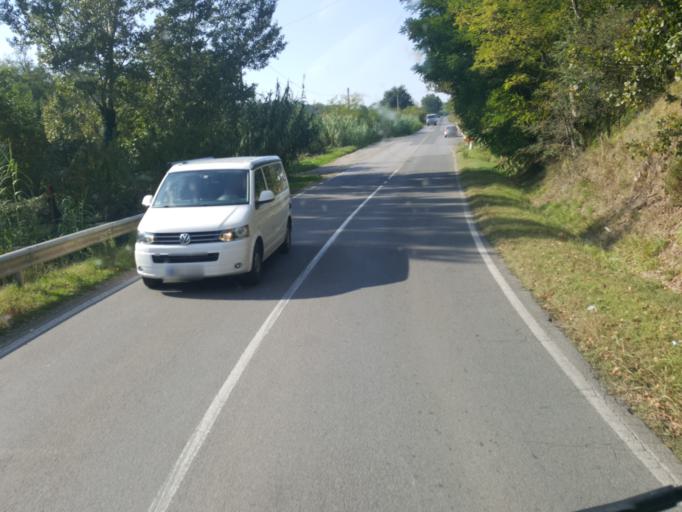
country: IT
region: Tuscany
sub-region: Provincia di Siena
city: Colle di Val d'Elsa
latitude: 43.4117
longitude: 11.1139
